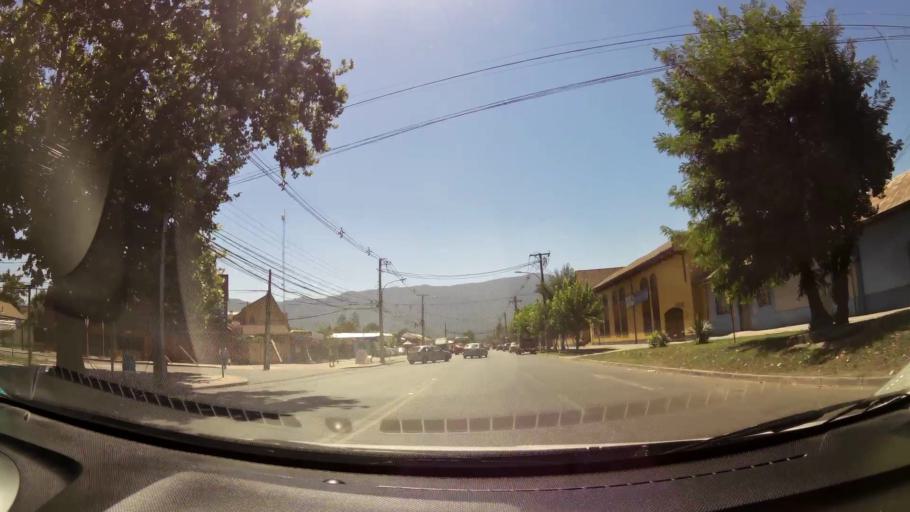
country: CL
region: O'Higgins
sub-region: Provincia de Colchagua
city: Chimbarongo
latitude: -34.5777
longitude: -70.9889
